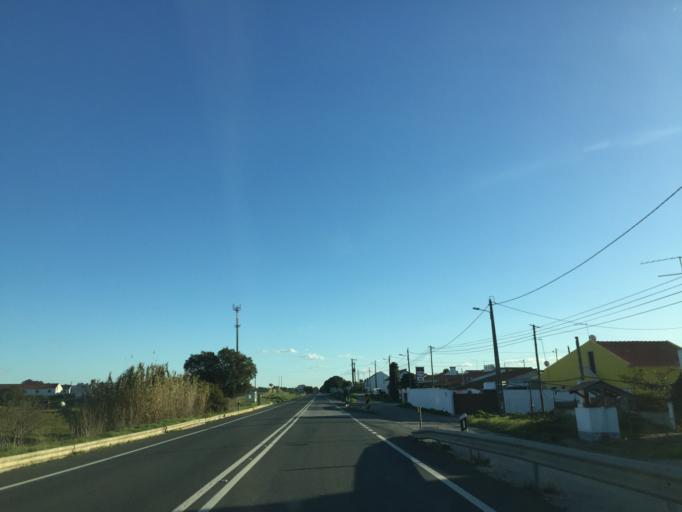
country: PT
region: Setubal
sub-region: Grandola
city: Grandola
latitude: 38.0502
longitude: -8.4022
